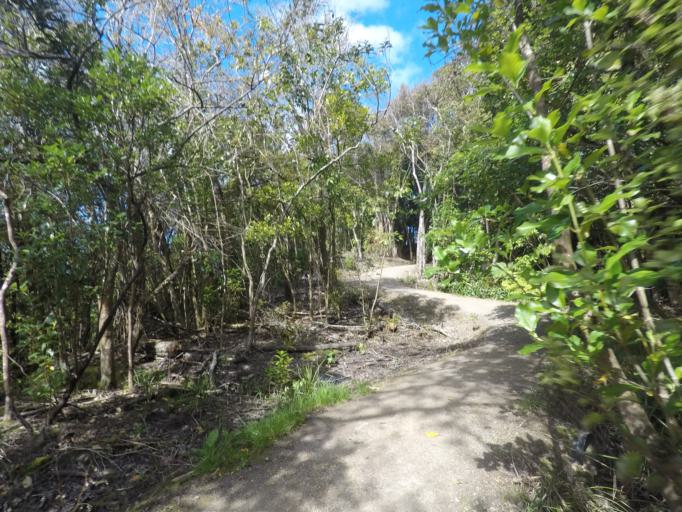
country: NZ
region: Auckland
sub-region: Auckland
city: Rosebank
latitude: -36.8571
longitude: 174.7162
